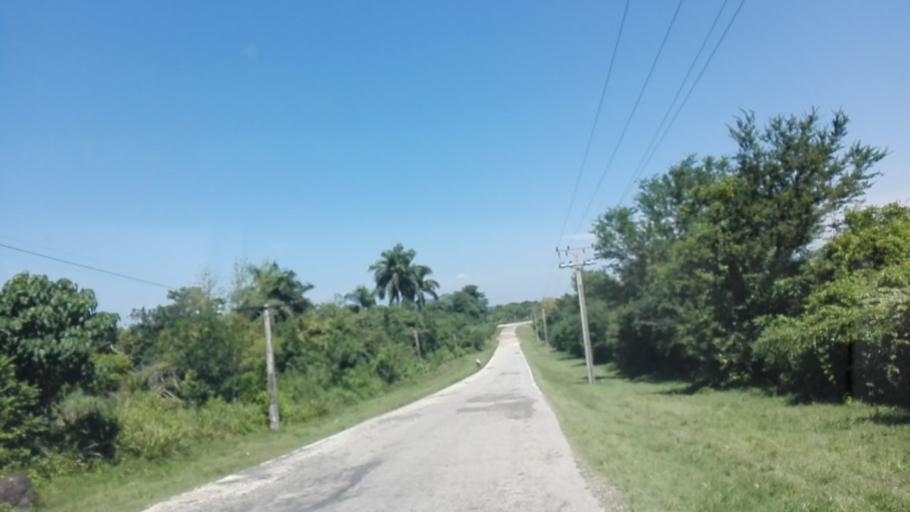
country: CU
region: Granma
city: Bartolome Maso
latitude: 20.1336
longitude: -76.9429
